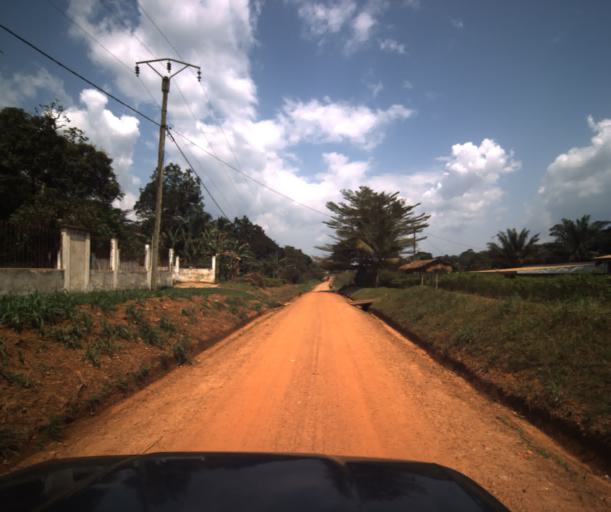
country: CM
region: Centre
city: Akono
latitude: 3.5503
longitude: 11.0531
